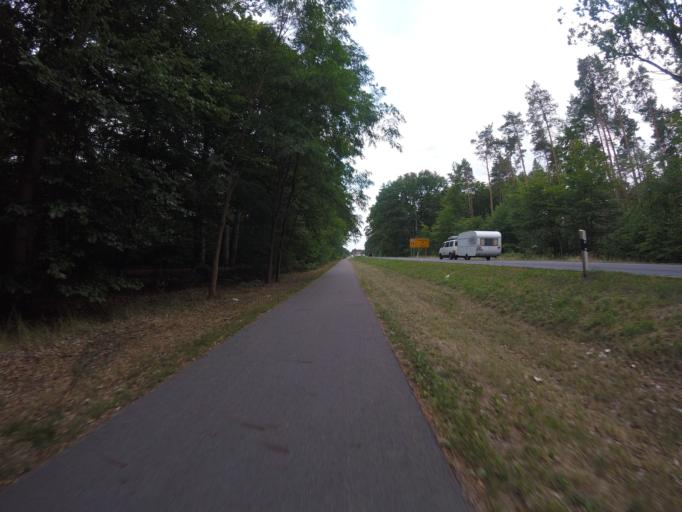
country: DE
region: Brandenburg
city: Oranienburg
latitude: 52.8012
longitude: 13.2300
